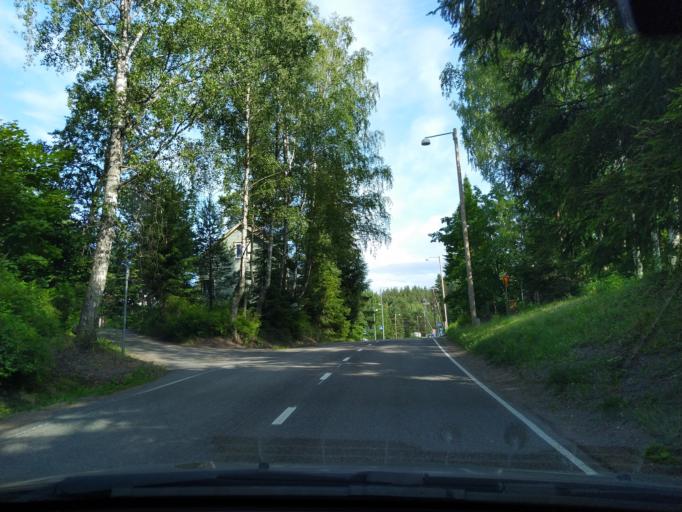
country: FI
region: Kymenlaakso
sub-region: Kouvola
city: Kouvola
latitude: 61.0909
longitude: 26.7927
